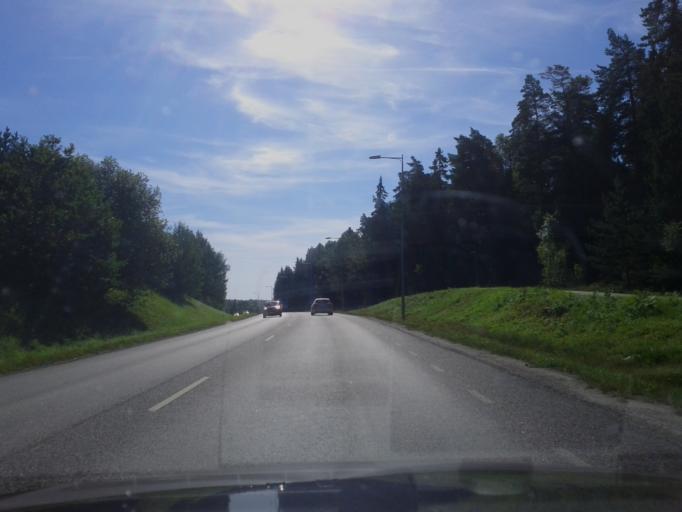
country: SE
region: Stockholm
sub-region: Taby Kommun
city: Taby
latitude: 59.4583
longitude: 18.0792
